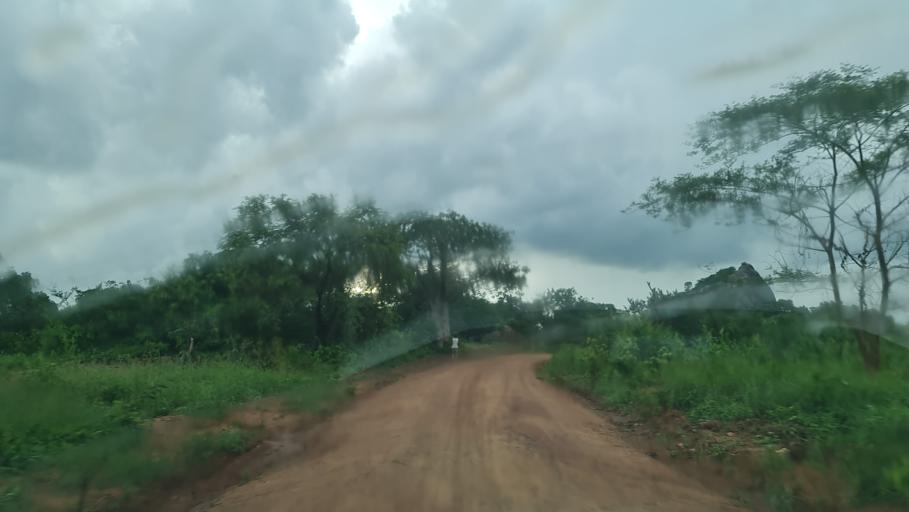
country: MZ
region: Nampula
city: Nacala
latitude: -13.9846
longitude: 40.3958
